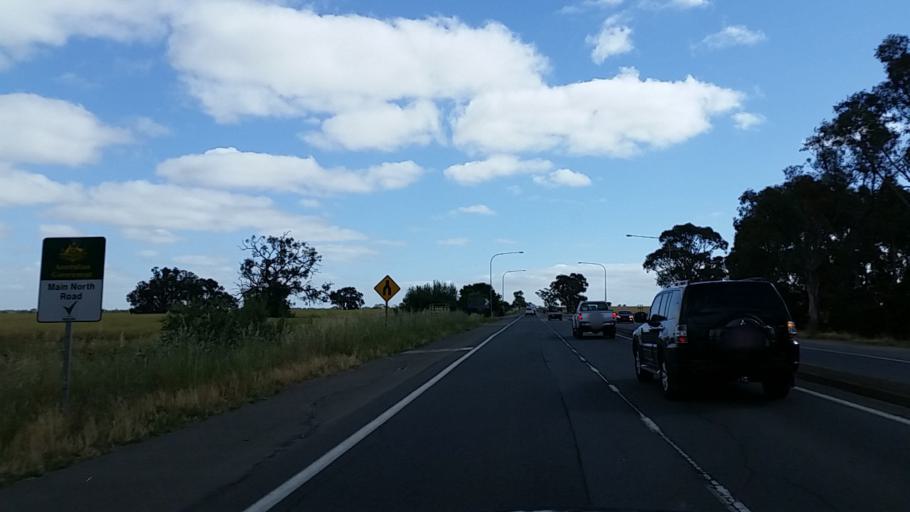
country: AU
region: South Australia
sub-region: Light
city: Willaston
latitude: -34.5677
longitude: 138.7461
